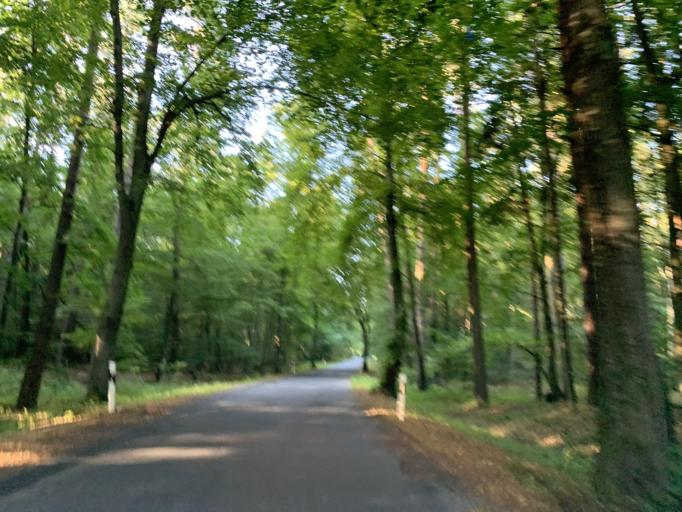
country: DE
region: Mecklenburg-Vorpommern
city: Carpin
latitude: 53.3419
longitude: 13.2416
